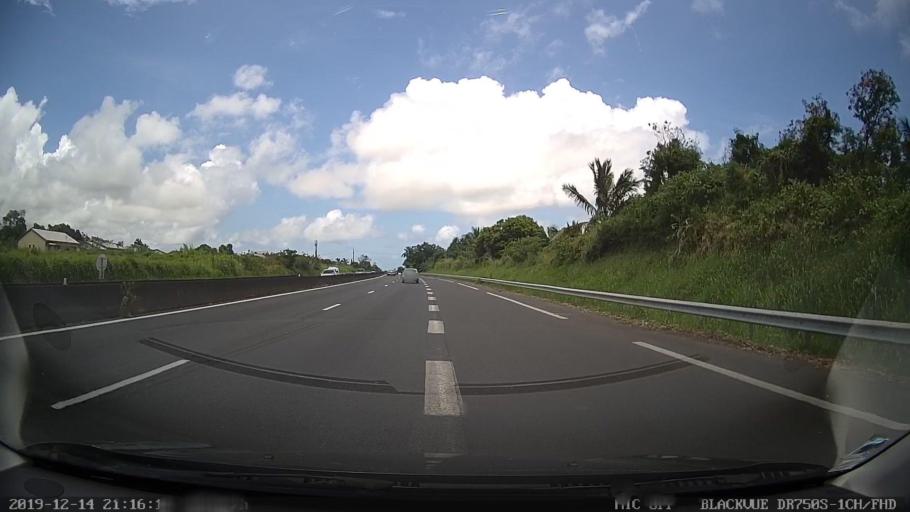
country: RE
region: Reunion
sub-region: Reunion
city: Saint-Andre
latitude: -20.9502
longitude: 55.6551
